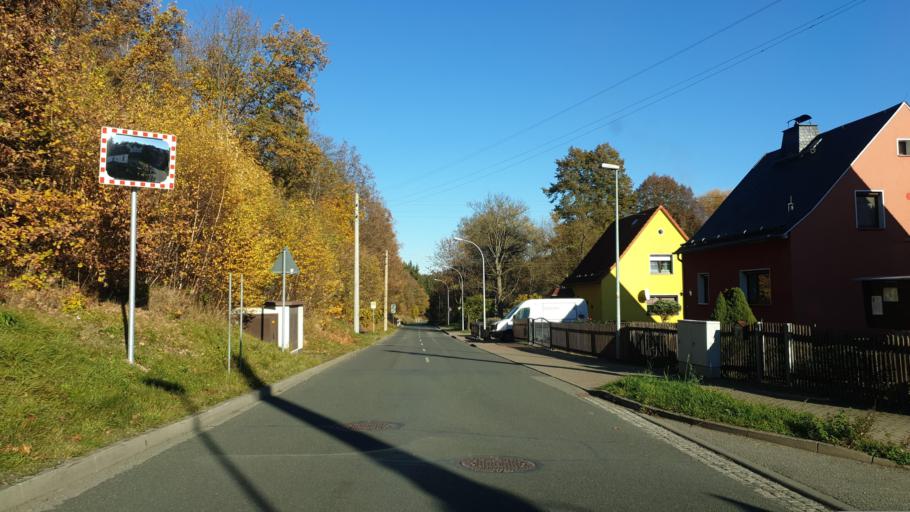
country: DE
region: Thuringia
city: Greiz
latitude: 50.6480
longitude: 12.1676
